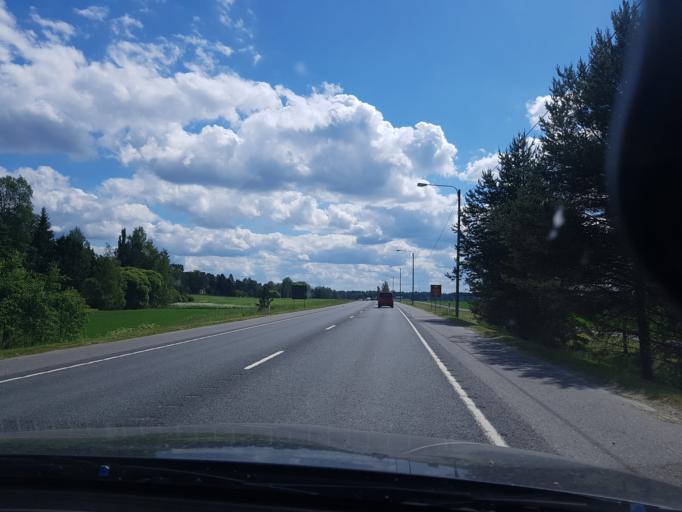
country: FI
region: Haeme
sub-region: Haemeenlinna
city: Parola
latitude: 61.0557
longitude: 24.3930
